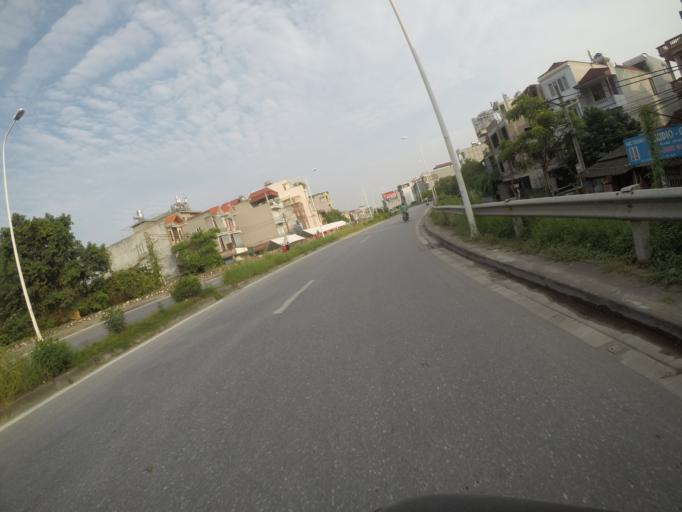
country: VN
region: Ha Noi
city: Tay Ho
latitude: 21.0896
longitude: 105.8130
